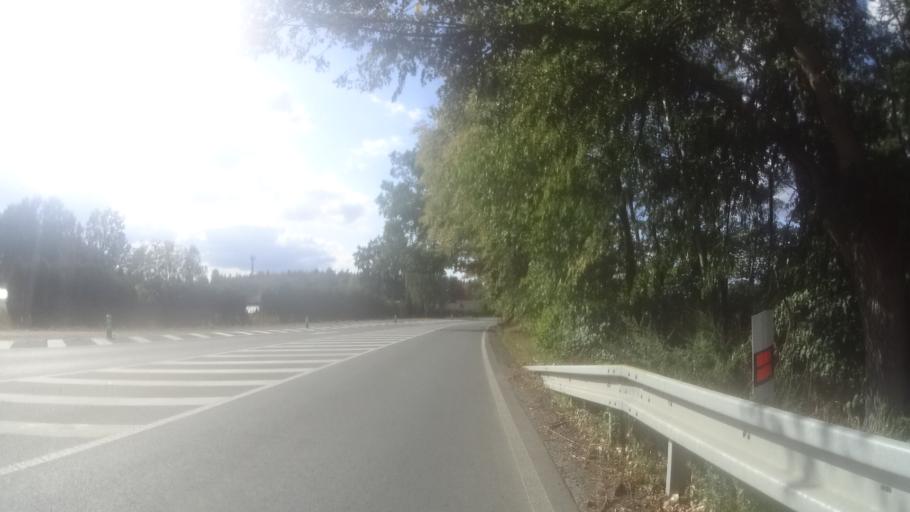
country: CZ
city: Borohradek
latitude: 50.1039
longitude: 16.0834
